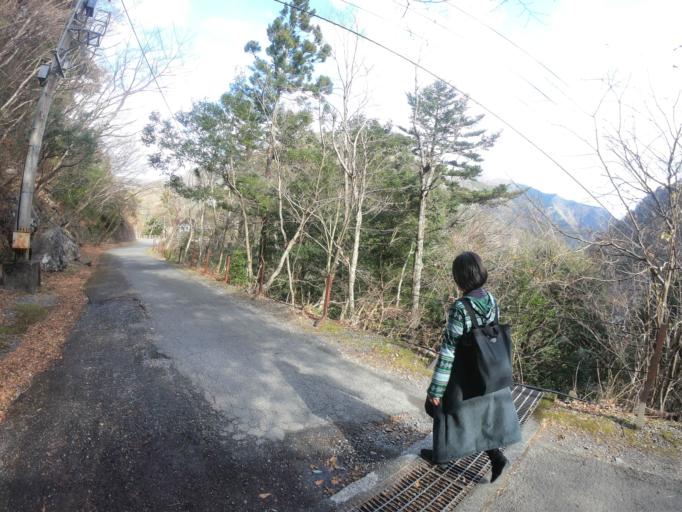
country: JP
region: Shizuoka
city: Shizuoka-shi
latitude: 35.1815
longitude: 138.1108
